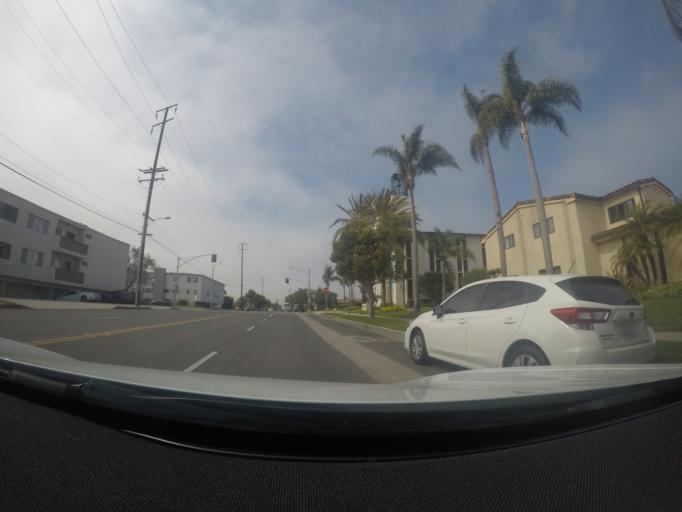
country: US
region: California
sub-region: Los Angeles County
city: Palos Verdes Estates
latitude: 33.8173
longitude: -118.3769
